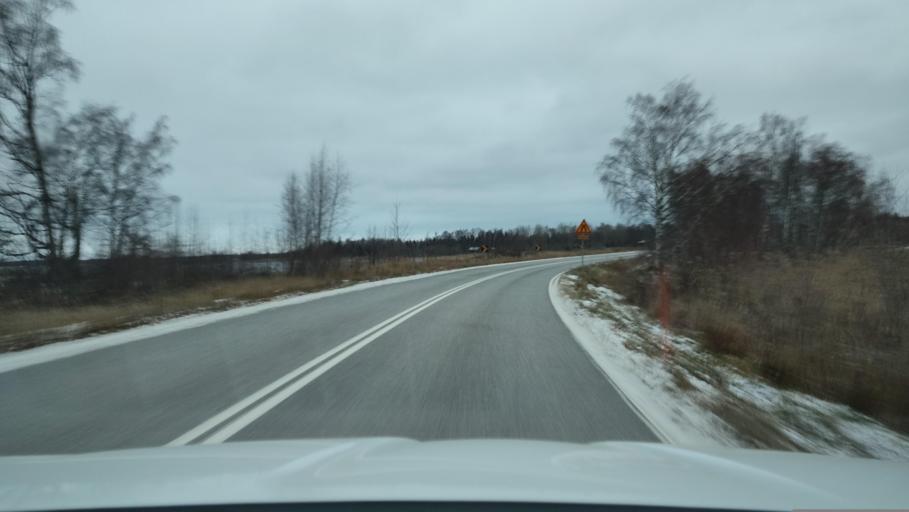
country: FI
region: Ostrobothnia
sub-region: Vaasa
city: Replot
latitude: 63.2864
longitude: 21.3330
